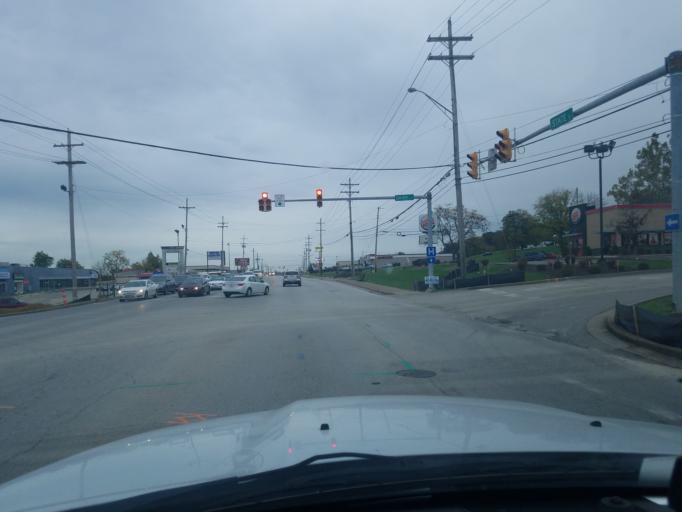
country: US
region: Indiana
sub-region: Floyd County
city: New Albany
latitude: 38.3092
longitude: -85.8440
